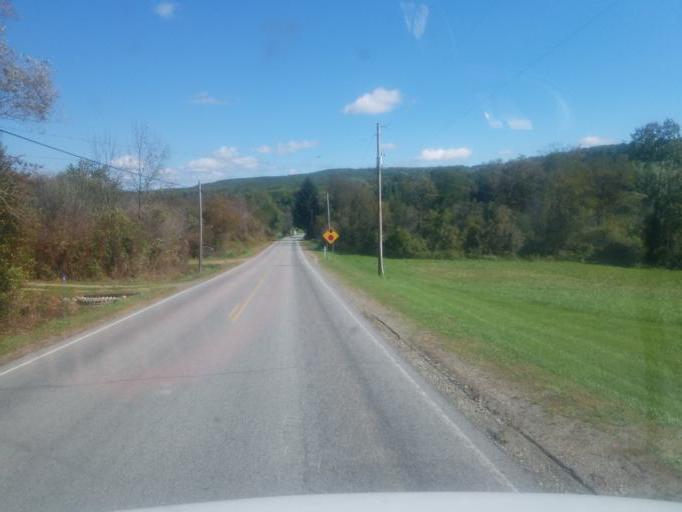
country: US
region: New York
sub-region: Allegany County
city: Friendship
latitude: 42.2778
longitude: -78.1334
